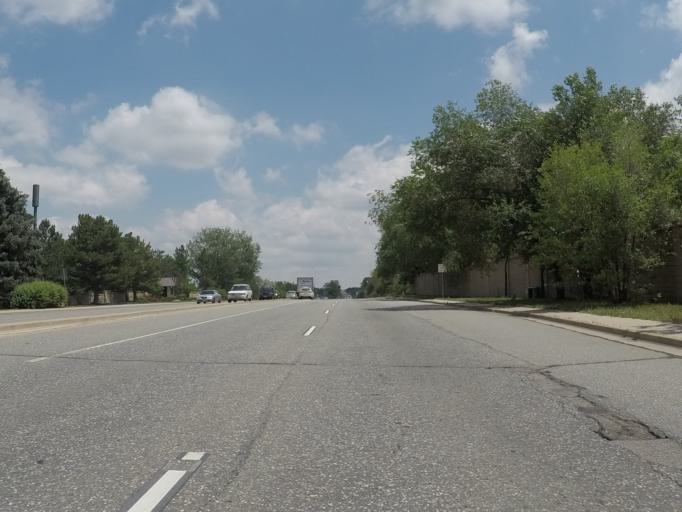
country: US
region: Colorado
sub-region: Arapahoe County
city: Greenwood Village
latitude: 39.6242
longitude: -104.9517
